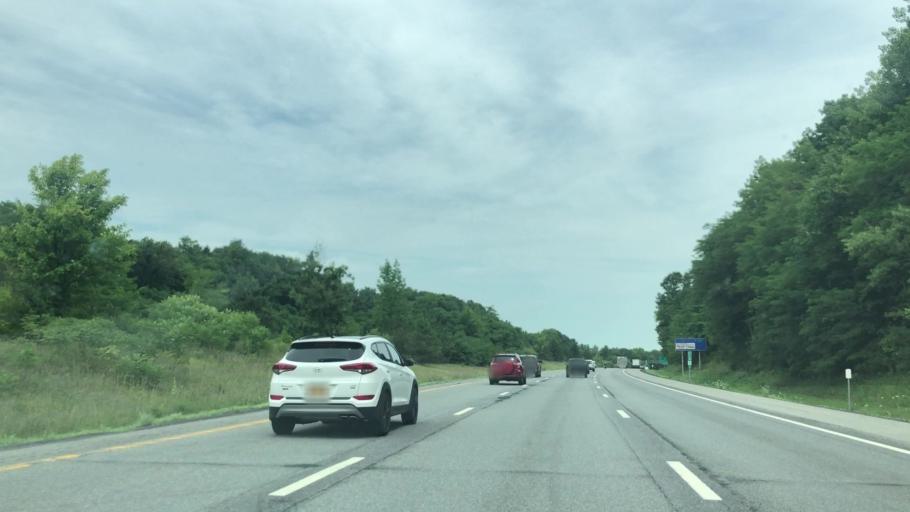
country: US
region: New York
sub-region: Saratoga County
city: Ballston Spa
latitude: 43.0139
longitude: -73.7985
